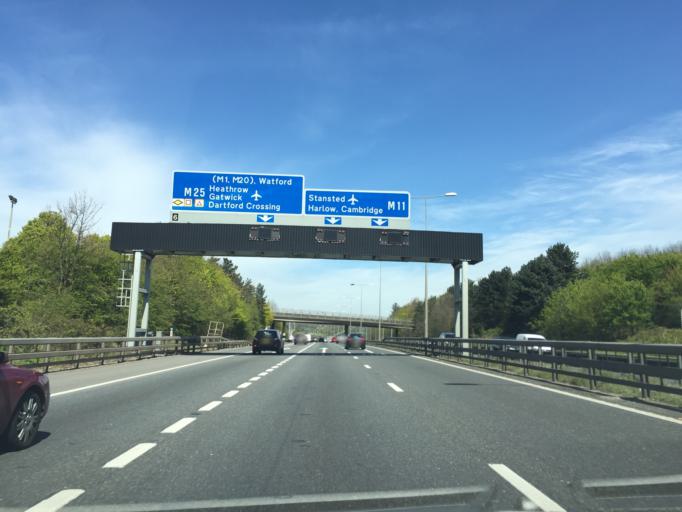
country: GB
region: England
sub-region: Essex
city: Theydon Bois
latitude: 51.6689
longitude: 0.1170
